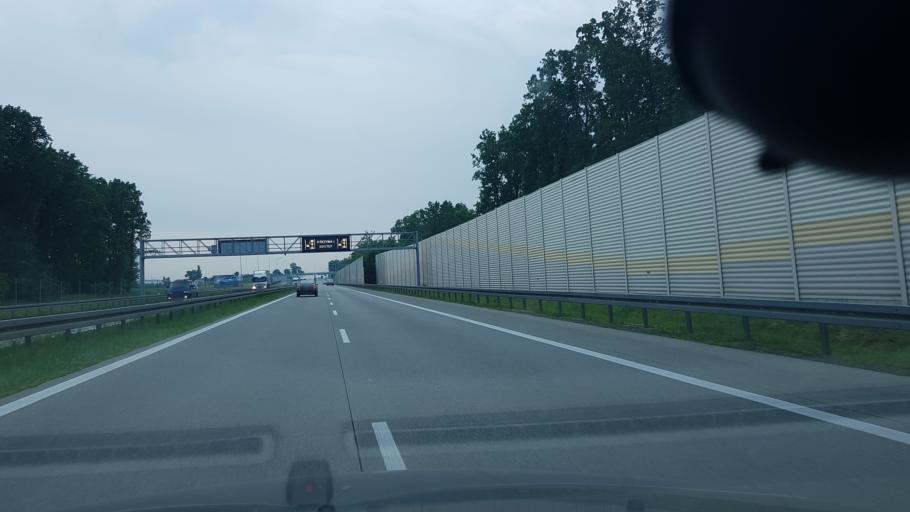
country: PL
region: Lodz Voivodeship
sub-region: Powiat rawski
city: Rawa Mazowiecka
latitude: 51.8094
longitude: 20.3068
